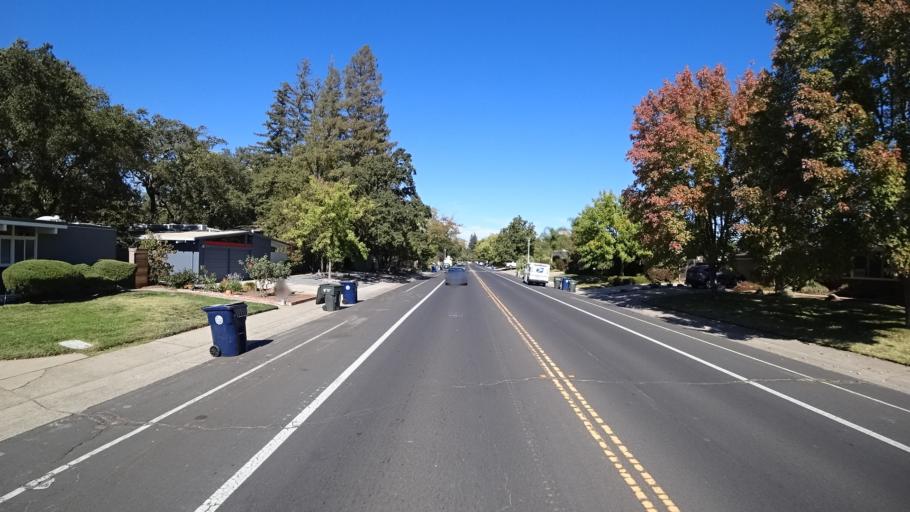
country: US
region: California
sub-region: Sacramento County
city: Parkway
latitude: 38.5118
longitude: -121.5156
